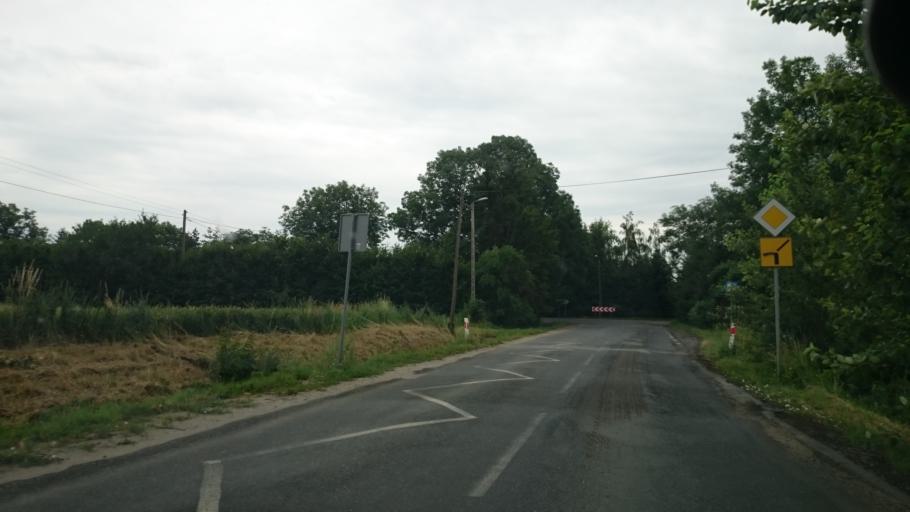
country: PL
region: Lower Silesian Voivodeship
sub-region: Powiat strzelinski
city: Przeworno
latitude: 50.6429
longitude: 17.2247
